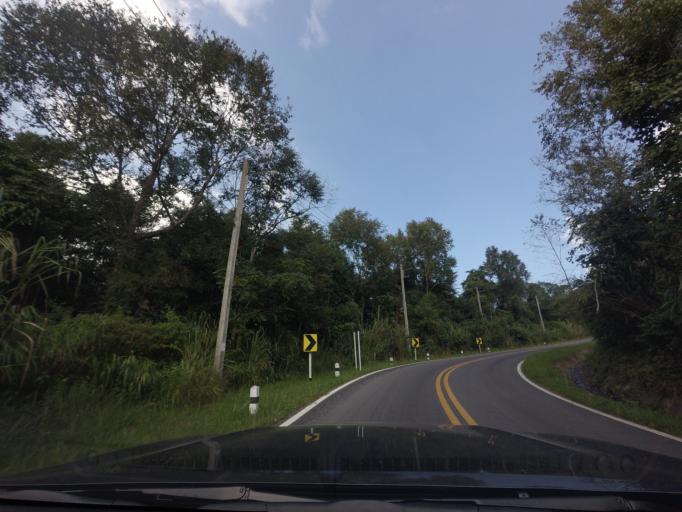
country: TH
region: Phitsanulok
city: Nakhon Thai
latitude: 16.9980
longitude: 101.0097
